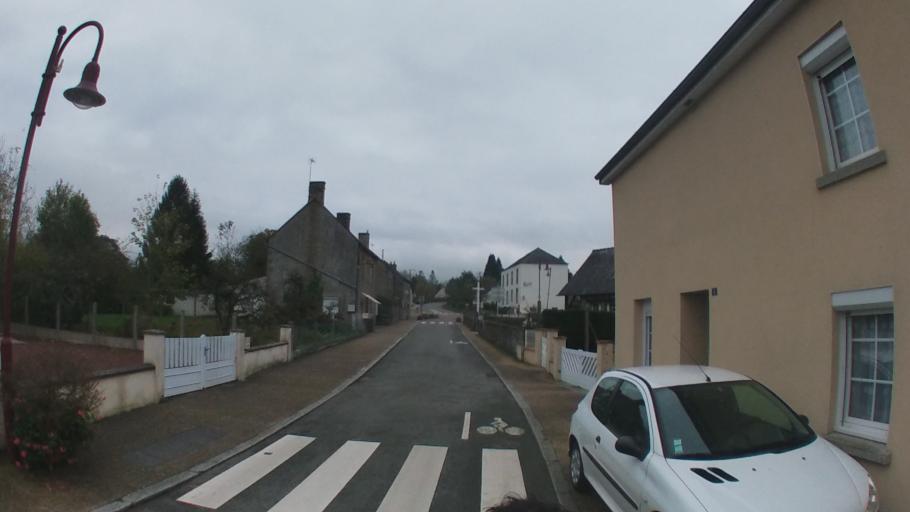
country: FR
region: Pays de la Loire
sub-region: Departement de la Mayenne
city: Aron
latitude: 48.3498
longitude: -0.5805
